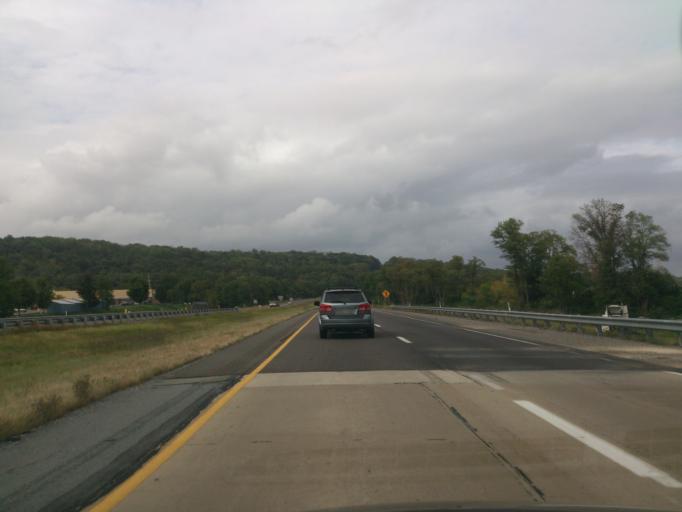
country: US
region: Pennsylvania
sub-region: Lancaster County
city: Ephrata
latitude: 40.1636
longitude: -76.1512
